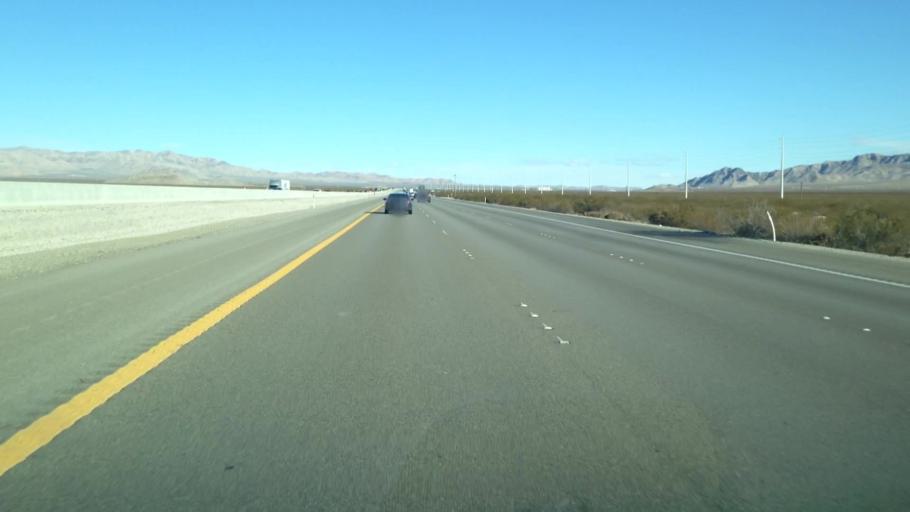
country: US
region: Nevada
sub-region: Clark County
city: Sandy Valley
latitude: 35.7018
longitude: -115.3698
